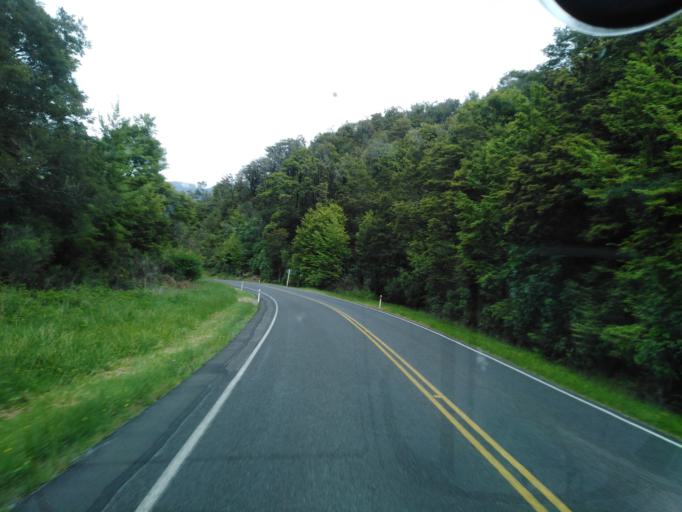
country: NZ
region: Tasman
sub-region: Tasman District
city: Wakefield
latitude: -41.7077
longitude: 172.5828
